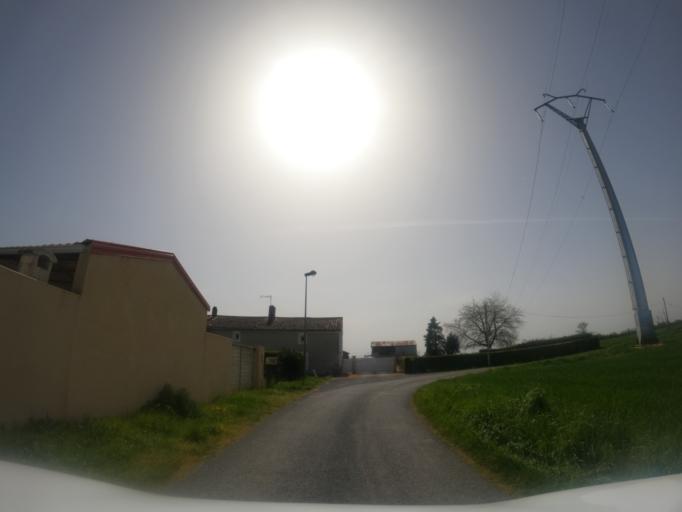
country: FR
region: Pays de la Loire
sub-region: Departement de la Vendee
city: Maillezais
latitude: 46.3869
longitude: -0.7944
